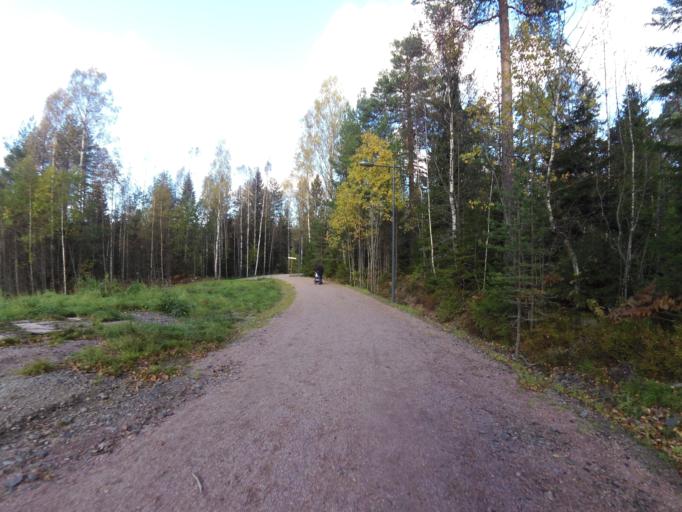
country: FI
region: Uusimaa
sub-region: Helsinki
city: Espoo
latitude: 60.1741
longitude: 24.6244
